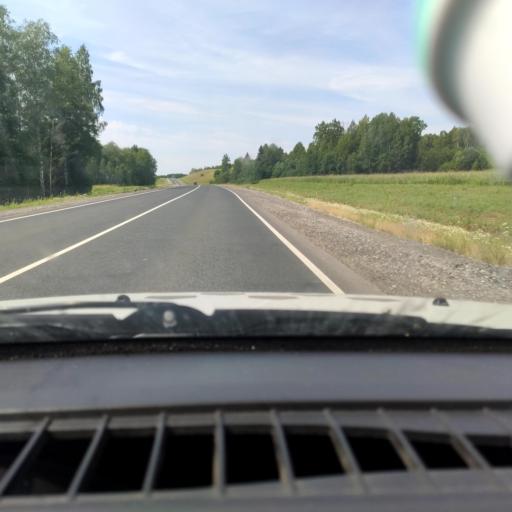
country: RU
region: Perm
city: Siva
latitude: 58.6352
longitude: 53.8551
